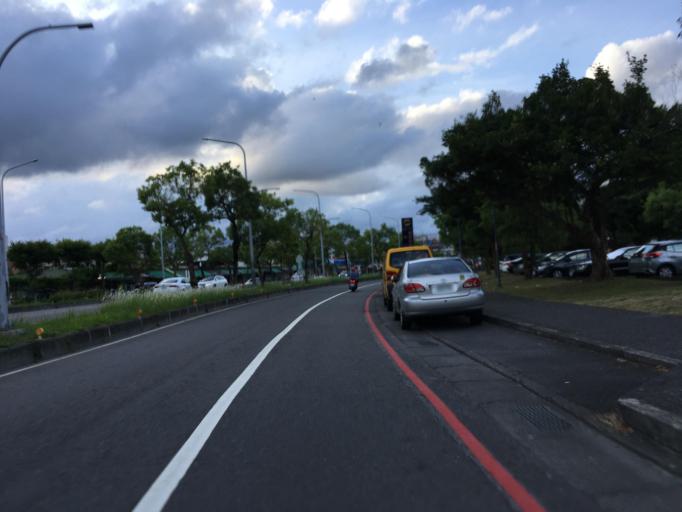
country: TW
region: Taiwan
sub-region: Yilan
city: Yilan
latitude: 24.6708
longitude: 121.7644
